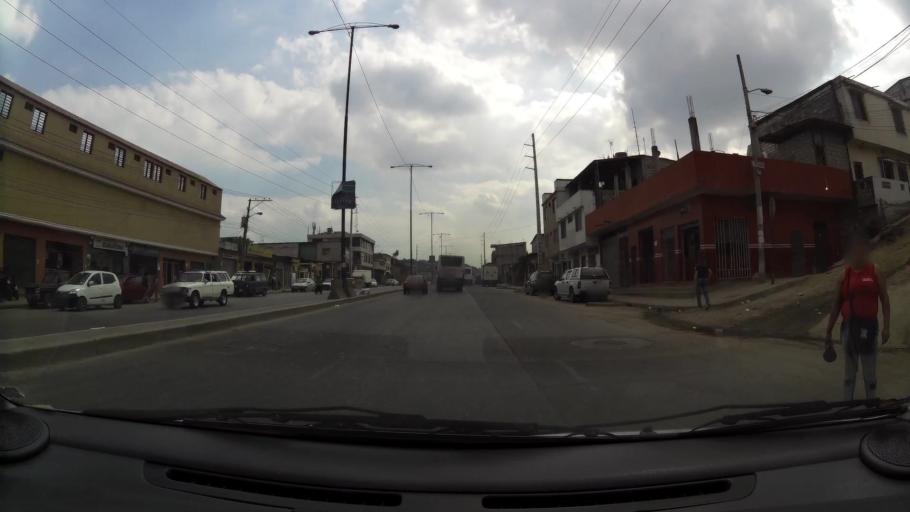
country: EC
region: Guayas
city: Santa Lucia
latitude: -2.1194
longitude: -79.9515
